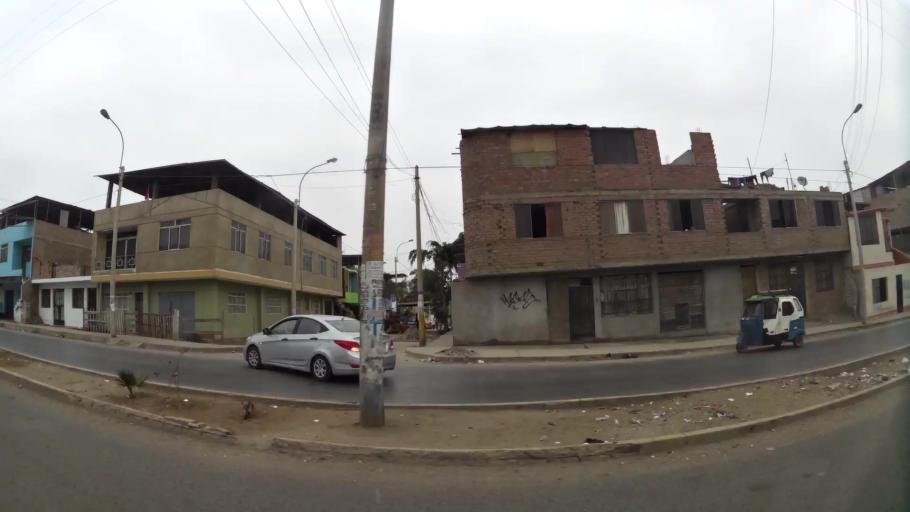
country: PE
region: Lima
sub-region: Lima
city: Surco
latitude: -12.2133
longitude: -76.9424
